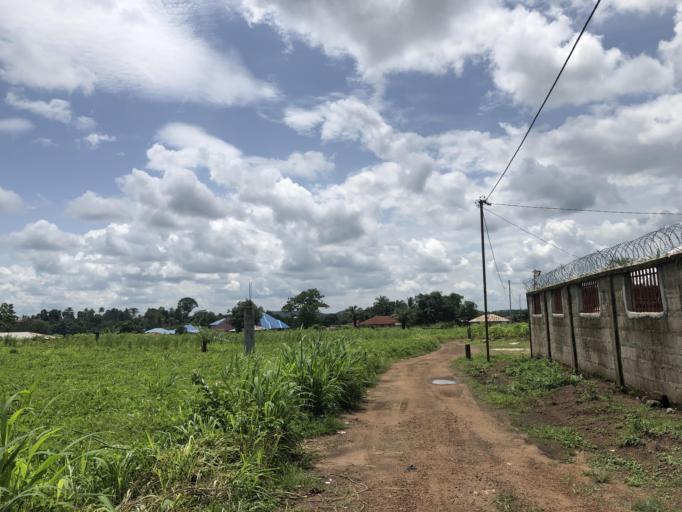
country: SL
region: Northern Province
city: Magburaka
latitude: 8.7050
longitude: -11.9239
